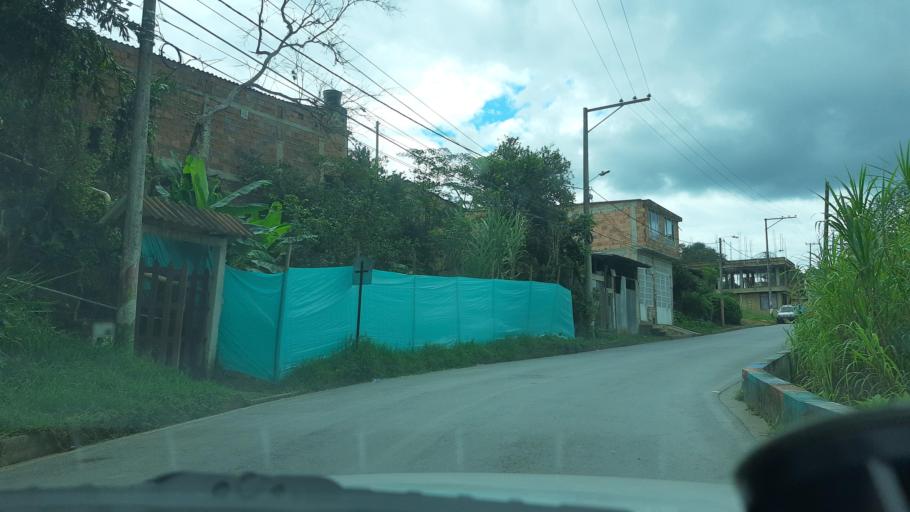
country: CO
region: Boyaca
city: Moniquira
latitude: 5.8803
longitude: -73.5732
